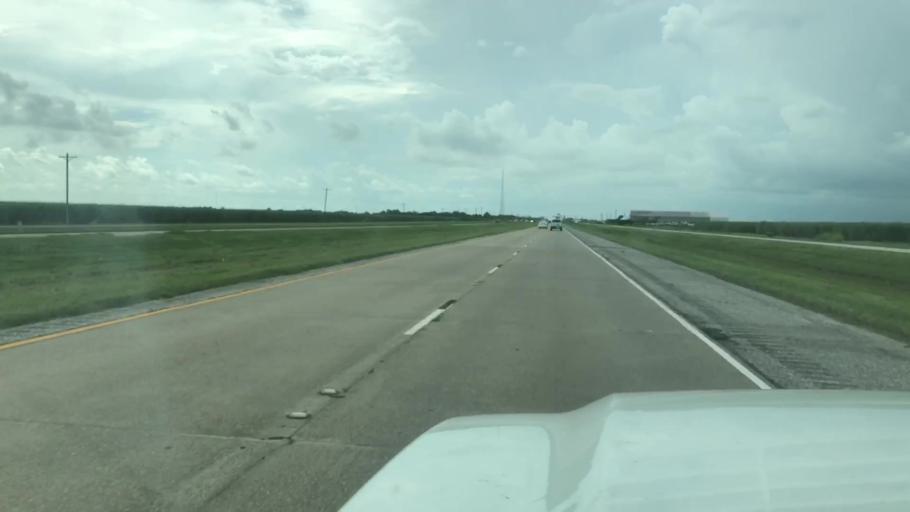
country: US
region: Louisiana
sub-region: Iberia Parish
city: Jeanerette
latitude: 29.9080
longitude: -91.7107
